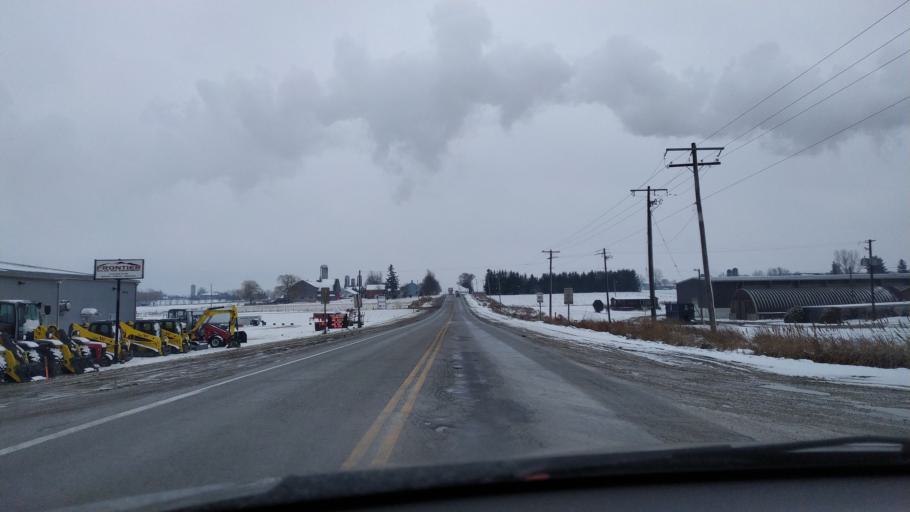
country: CA
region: Ontario
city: Waterloo
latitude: 43.5953
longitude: -80.6236
